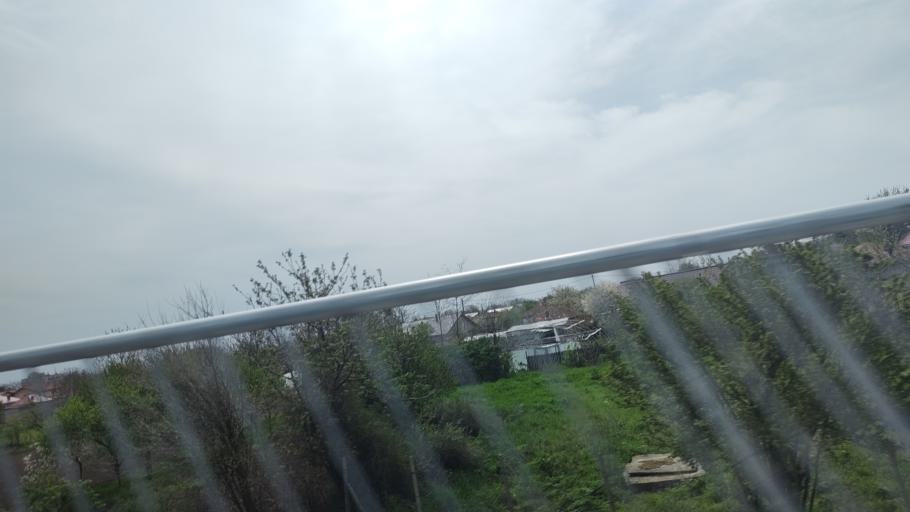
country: RO
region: Constanta
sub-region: Comuna Cobadin
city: Cobadin
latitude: 44.0702
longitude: 28.2251
